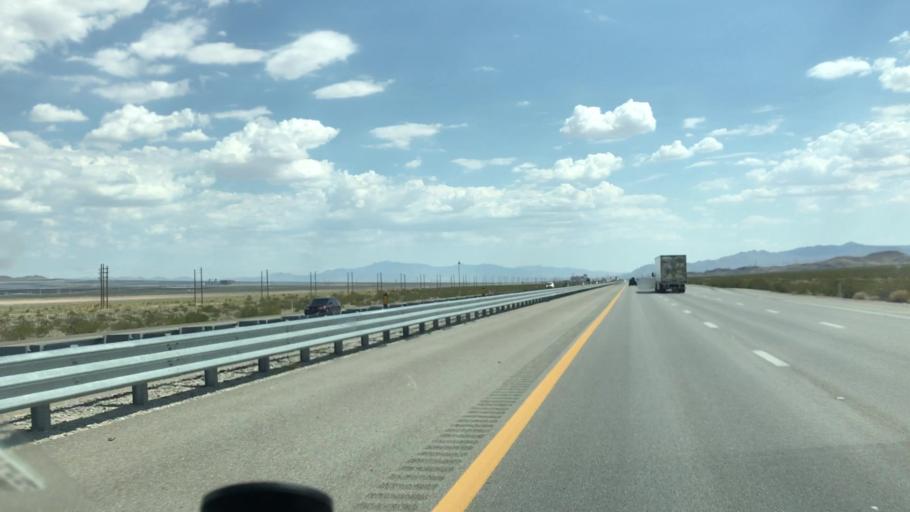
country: US
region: Nevada
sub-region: Clark County
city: Sandy Valley
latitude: 35.6678
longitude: -115.3790
